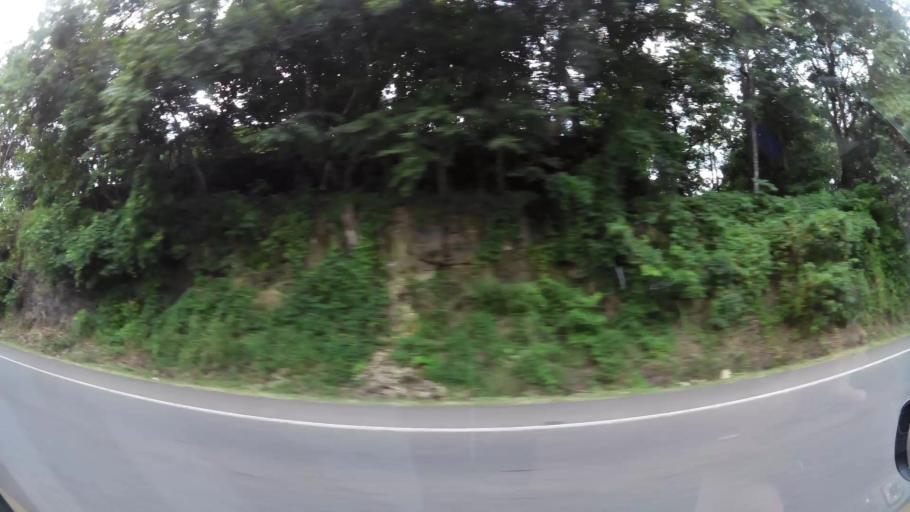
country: CR
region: Alajuela
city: Orotina
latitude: 9.8727
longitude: -84.5732
